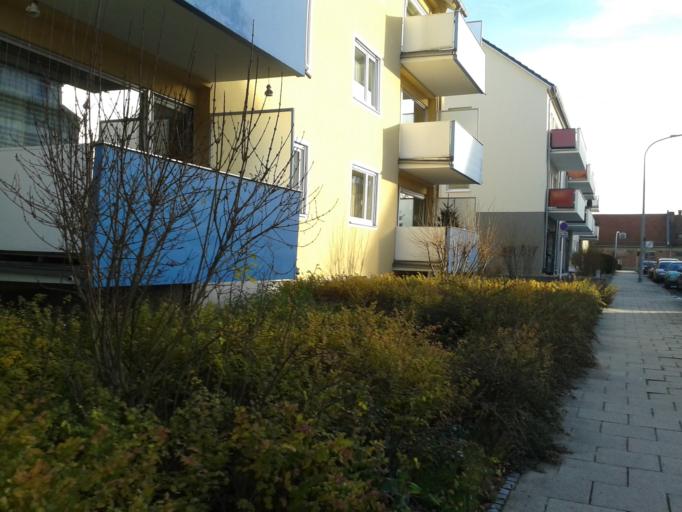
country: DE
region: Bavaria
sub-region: Upper Franconia
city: Bamberg
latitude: 49.9084
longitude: 10.9172
